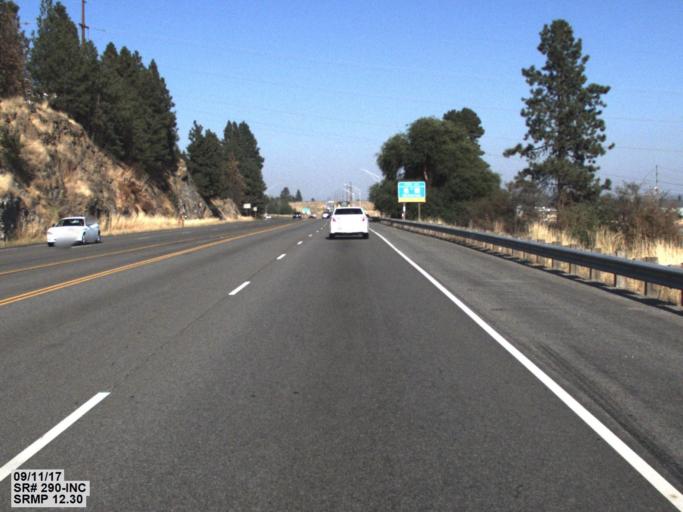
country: US
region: Washington
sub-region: Spokane County
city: Liberty Lake
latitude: 47.6989
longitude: -117.1594
